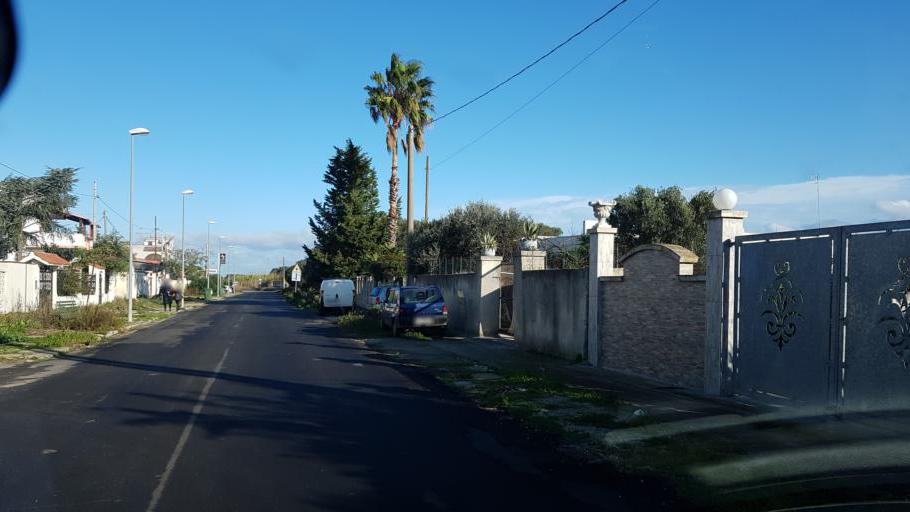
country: IT
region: Apulia
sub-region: Provincia di Brindisi
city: Tuturano
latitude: 40.5475
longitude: 17.9472
